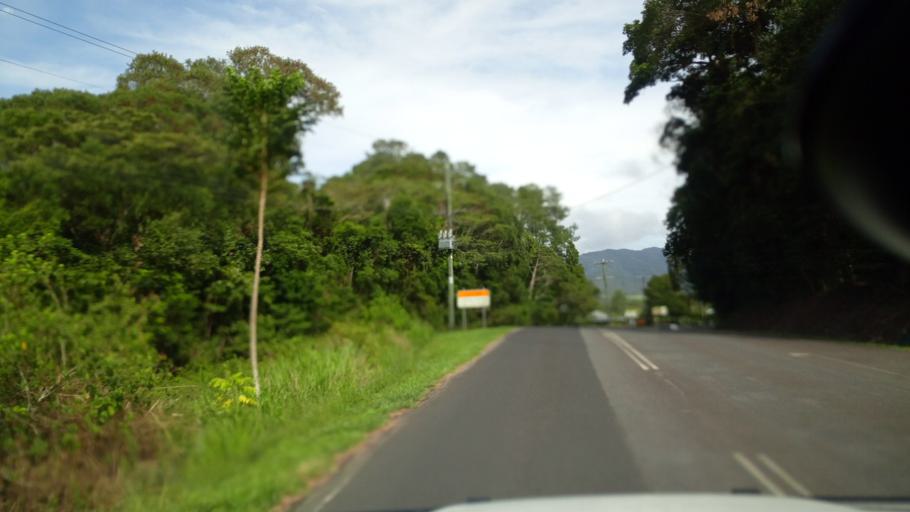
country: AU
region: Queensland
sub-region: Tablelands
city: Kuranda
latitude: -16.8216
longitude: 145.6240
